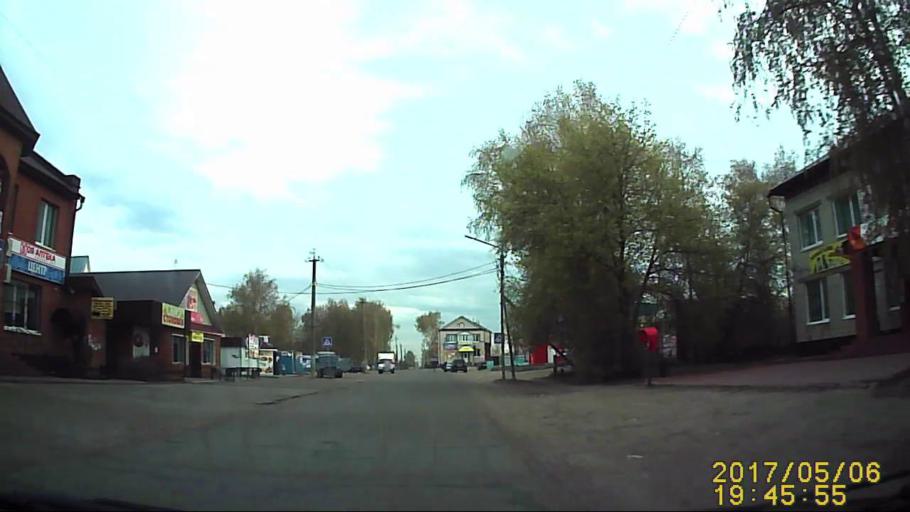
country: RU
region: Ulyanovsk
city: Staraya Mayna
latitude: 54.6064
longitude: 48.9228
